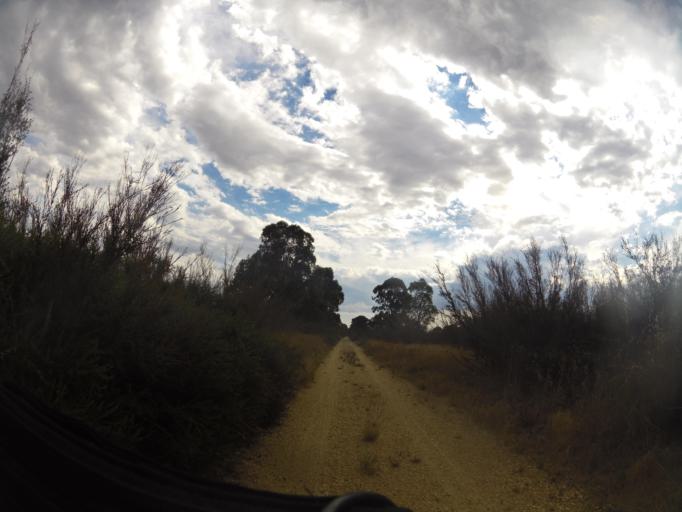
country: AU
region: Victoria
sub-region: Wellington
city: Heyfield
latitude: -38.0423
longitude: 146.6438
